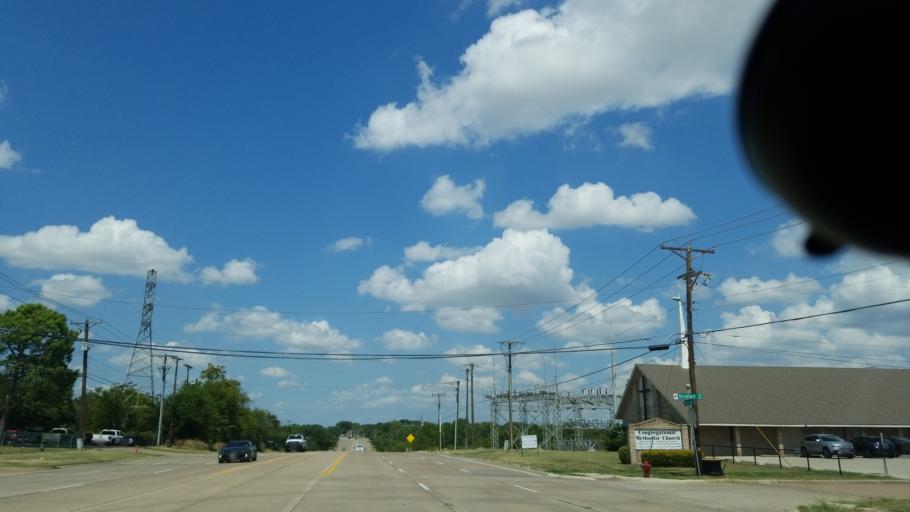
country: US
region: Texas
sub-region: Dallas County
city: Grand Prairie
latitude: 32.7283
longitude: -96.9941
